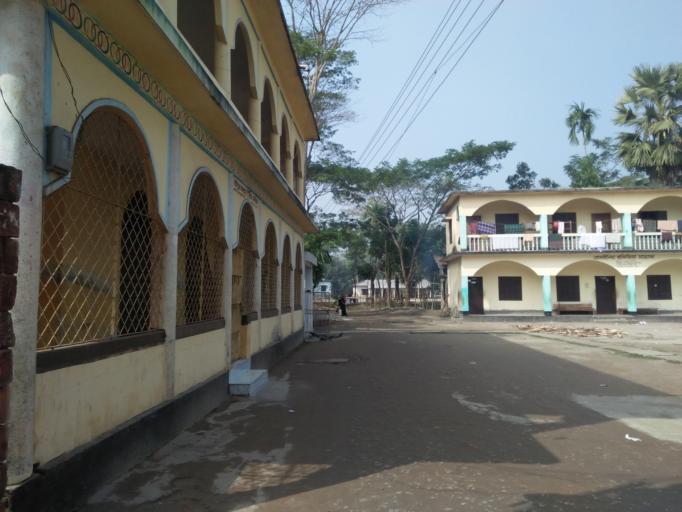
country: BD
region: Barisal
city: Bhola
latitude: 22.6802
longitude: 90.6373
